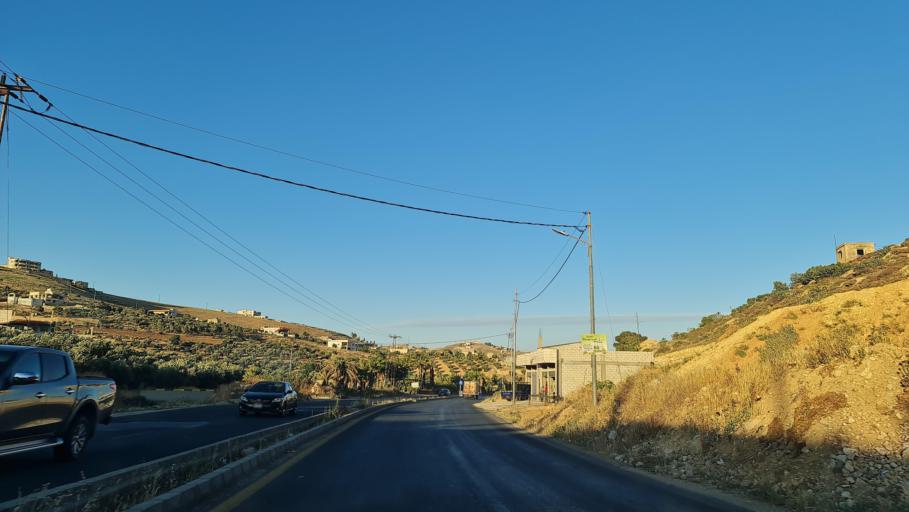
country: JO
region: Amman
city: Al Jubayhah
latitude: 32.0927
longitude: 35.9387
